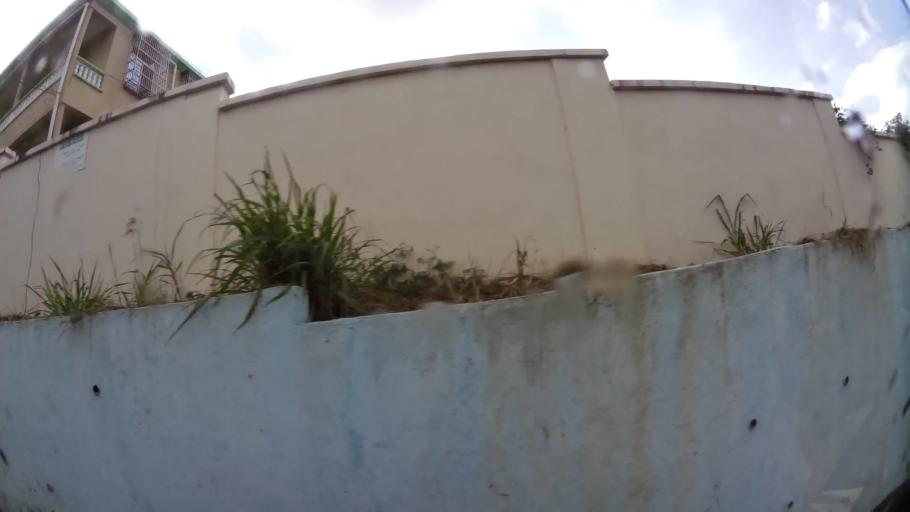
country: DM
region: Saint George
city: Roseau
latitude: 15.3259
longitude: -61.3911
